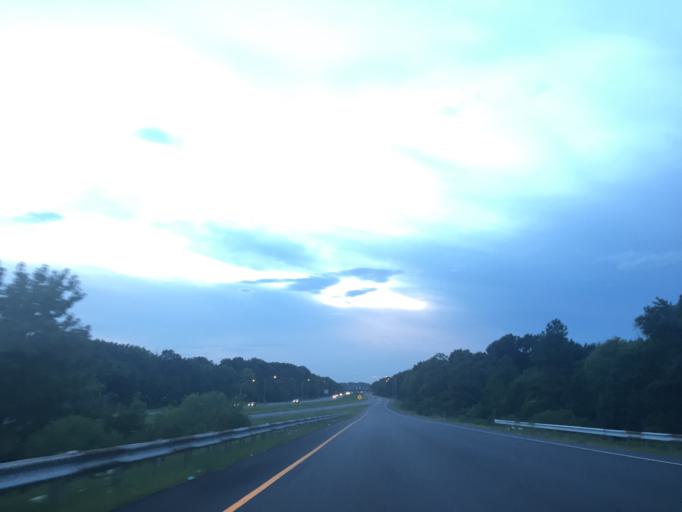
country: US
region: Maryland
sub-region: Baltimore County
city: Essex
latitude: 39.2790
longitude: -76.4734
